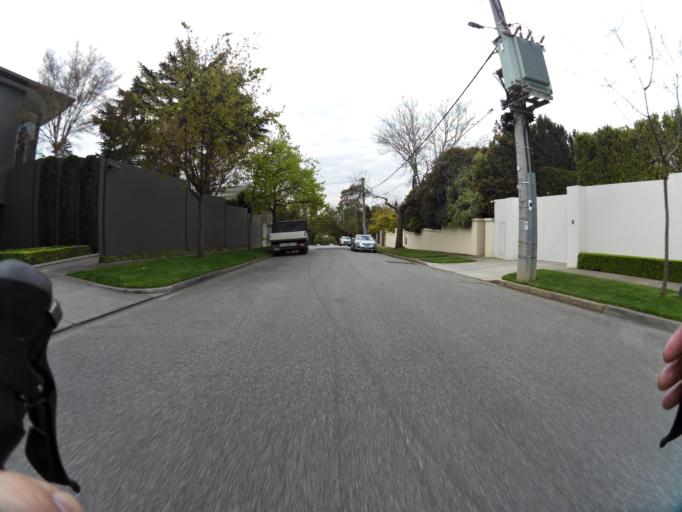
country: AU
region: Victoria
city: Toorak
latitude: -37.8449
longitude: 145.0257
